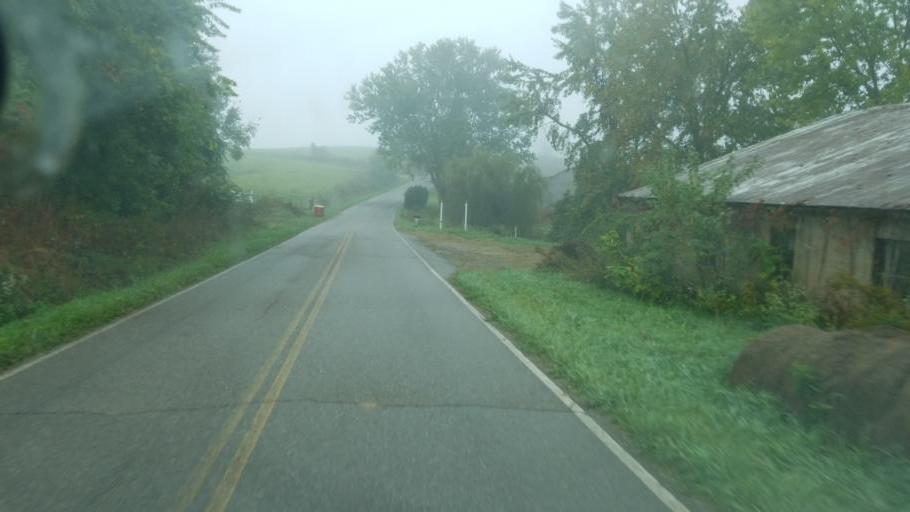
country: US
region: Ohio
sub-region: Harrison County
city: Cadiz
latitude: 40.3848
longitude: -81.1108
